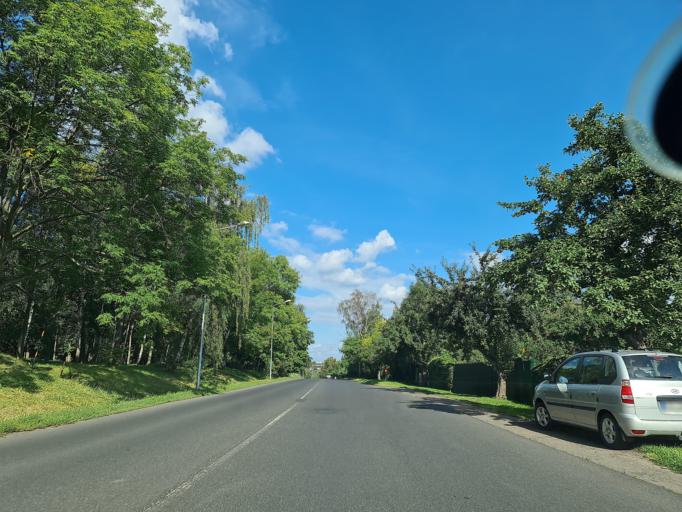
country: CZ
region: Ustecky
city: Mezibori
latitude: 50.5935
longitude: 13.5808
